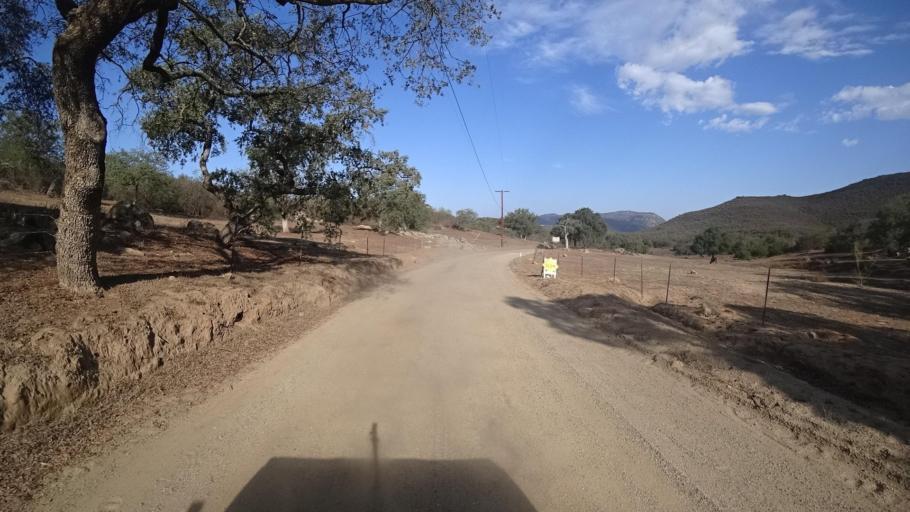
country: US
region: California
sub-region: San Diego County
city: San Pasqual
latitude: 33.1678
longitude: -116.9591
